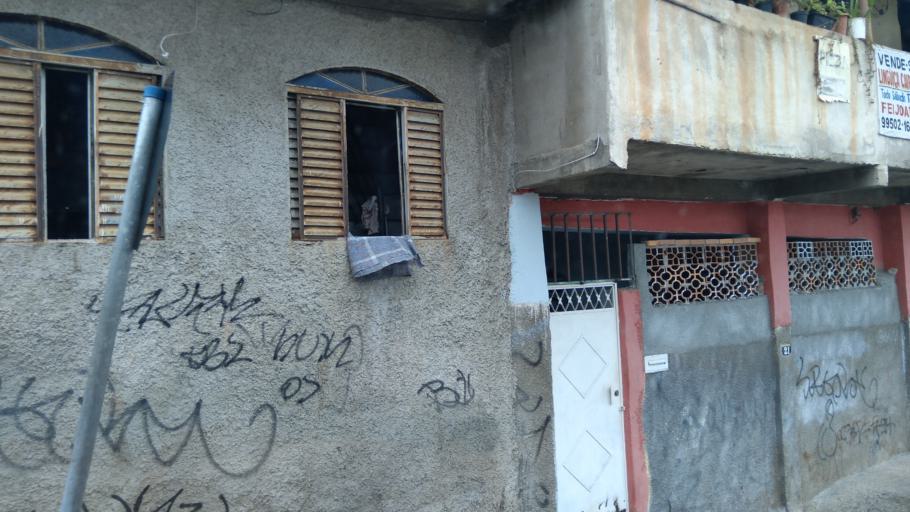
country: BR
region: Minas Gerais
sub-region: Belo Horizonte
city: Belo Horizonte
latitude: -19.8928
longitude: -43.9001
